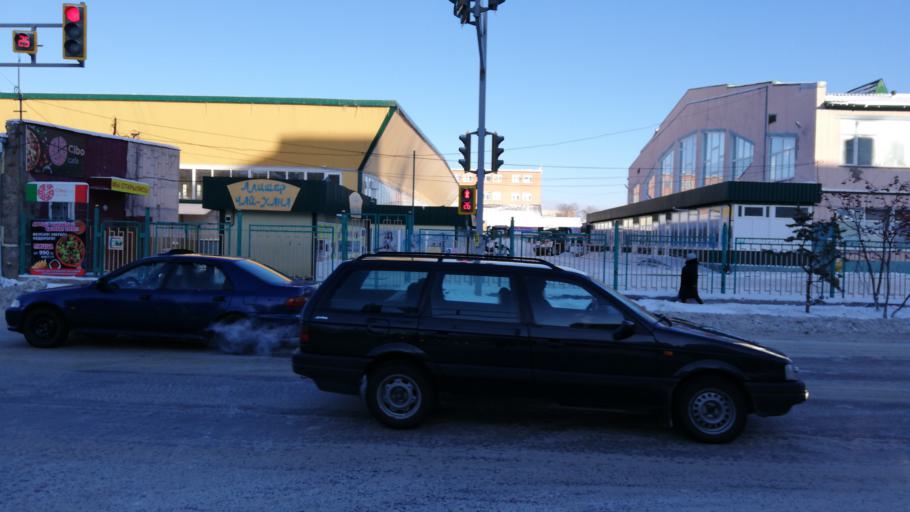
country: KZ
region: Soltustik Qazaqstan
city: Petropavlovsk
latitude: 54.8629
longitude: 69.1465
